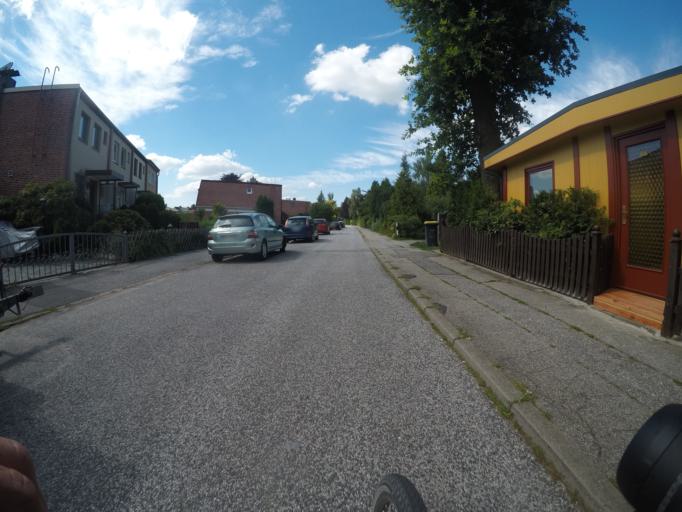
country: DE
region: Schleswig-Holstein
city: Glinde
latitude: 53.4995
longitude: 10.1794
